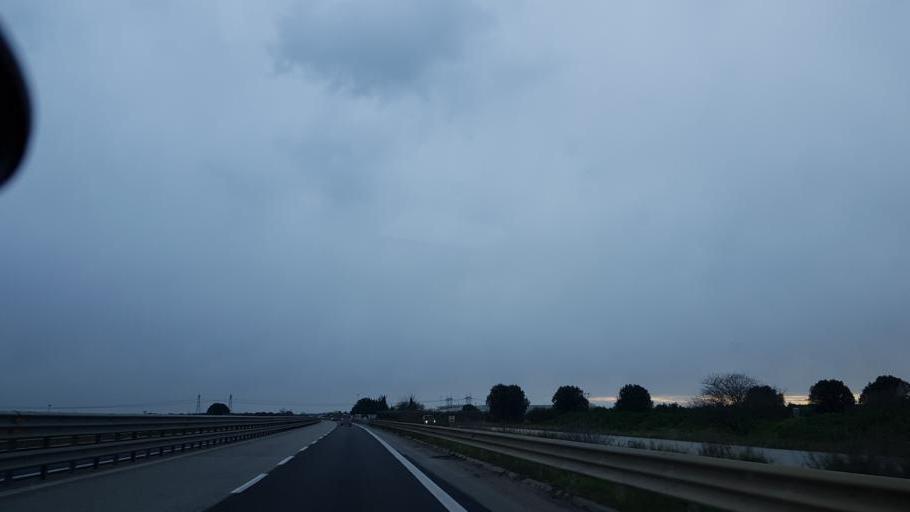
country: IT
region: Apulia
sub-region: Provincia di Brindisi
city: Mesagne
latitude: 40.5838
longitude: 17.8473
